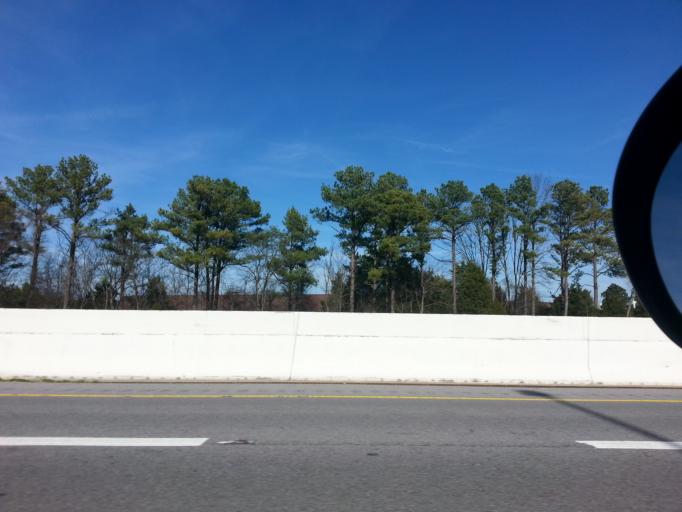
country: US
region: Tennessee
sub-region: Rutherford County
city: Murfreesboro
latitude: 35.8319
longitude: -86.4185
